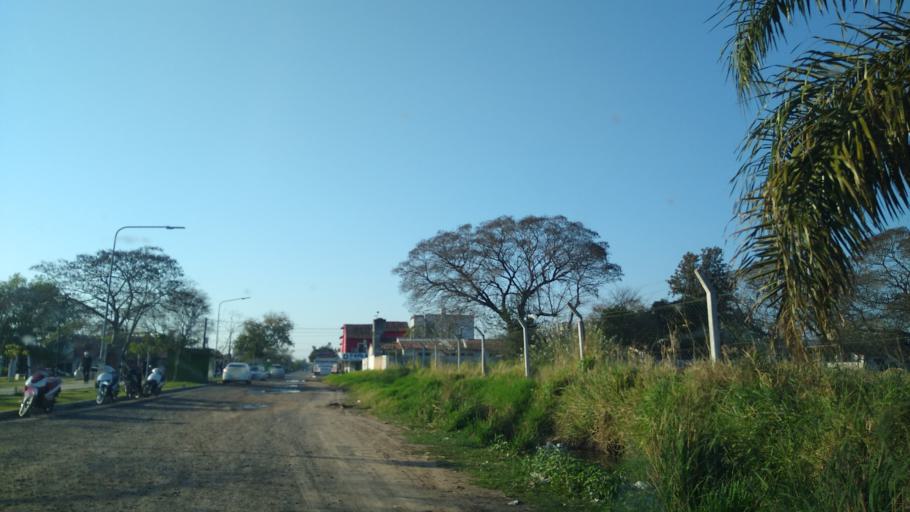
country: AR
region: Chaco
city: Barranqueras
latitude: -27.4831
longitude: -58.9523
